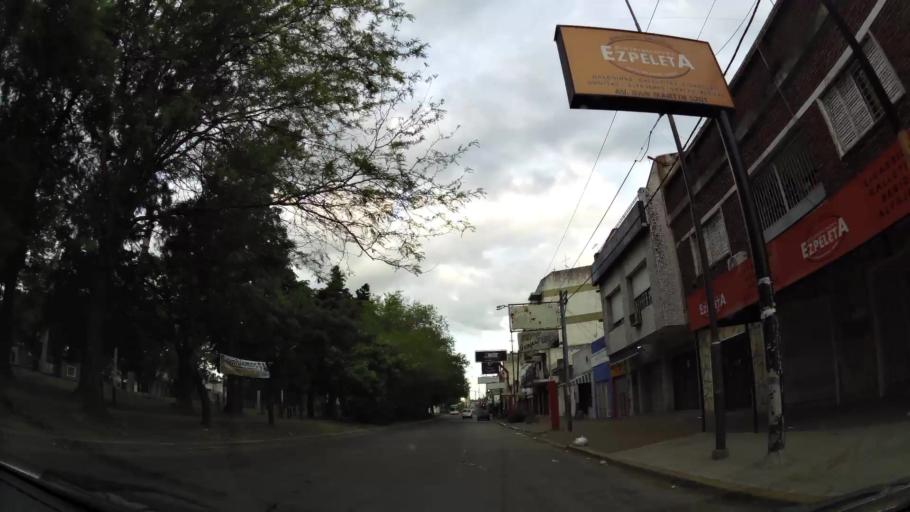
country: AR
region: Buenos Aires
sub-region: Partido de Quilmes
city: Quilmes
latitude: -34.7511
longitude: -58.2363
